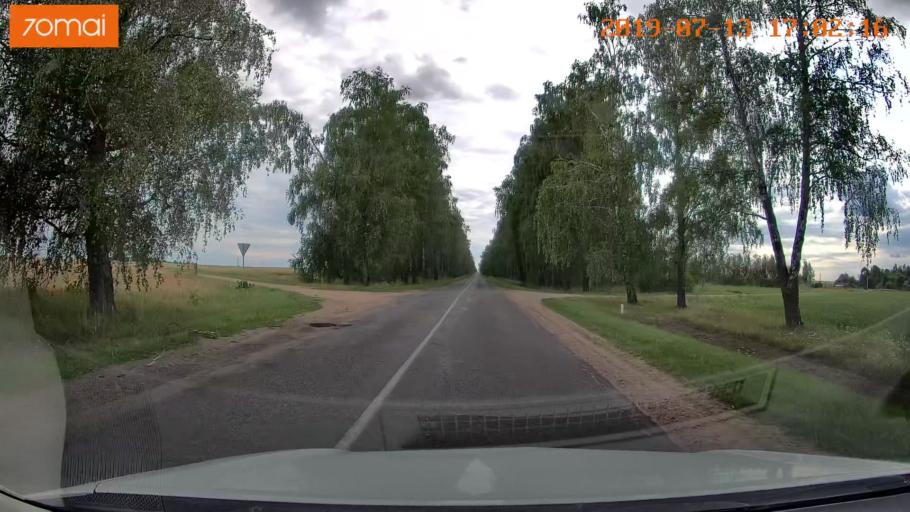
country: BY
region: Mogilev
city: Kirawsk
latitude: 53.2876
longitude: 29.3885
